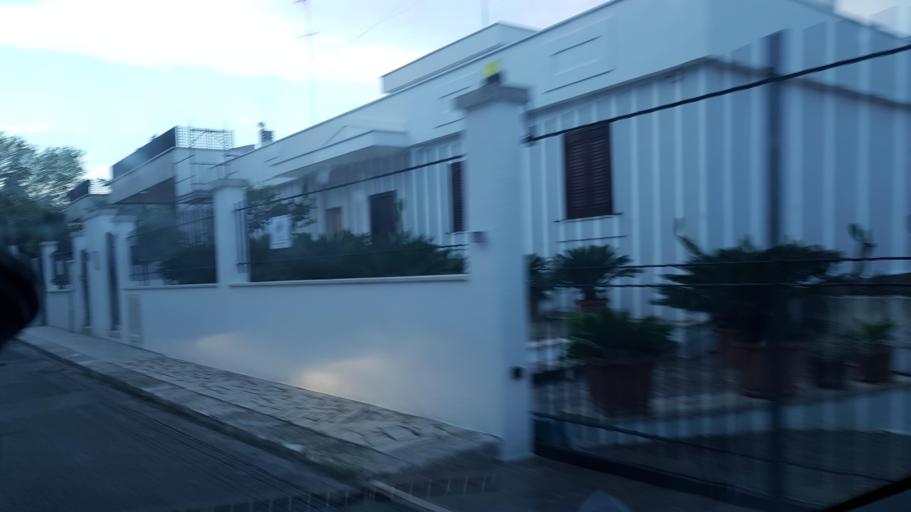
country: IT
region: Apulia
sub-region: Provincia di Brindisi
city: Ceglie Messapica
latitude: 40.6489
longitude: 17.5155
